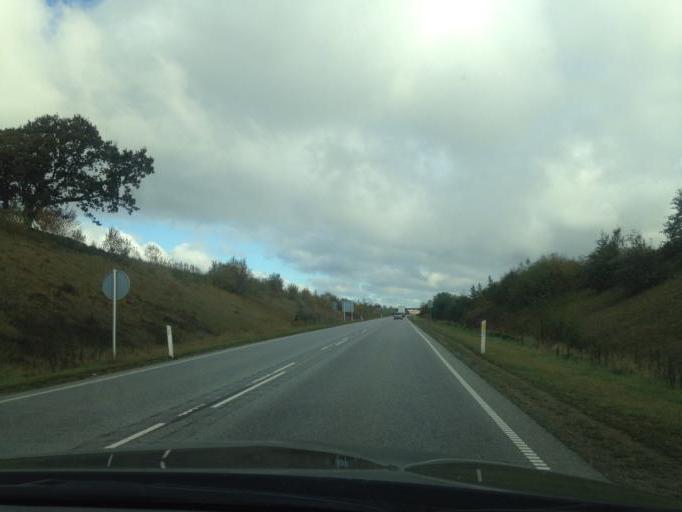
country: DK
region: South Denmark
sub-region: Vejle Kommune
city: Give
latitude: 55.8295
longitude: 9.2575
